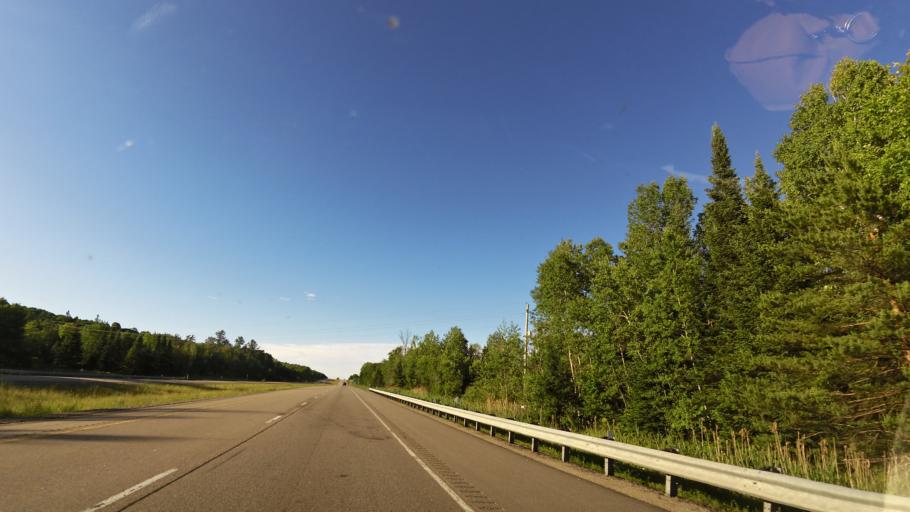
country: CA
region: Ontario
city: Orillia
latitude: 44.6412
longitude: -79.6525
